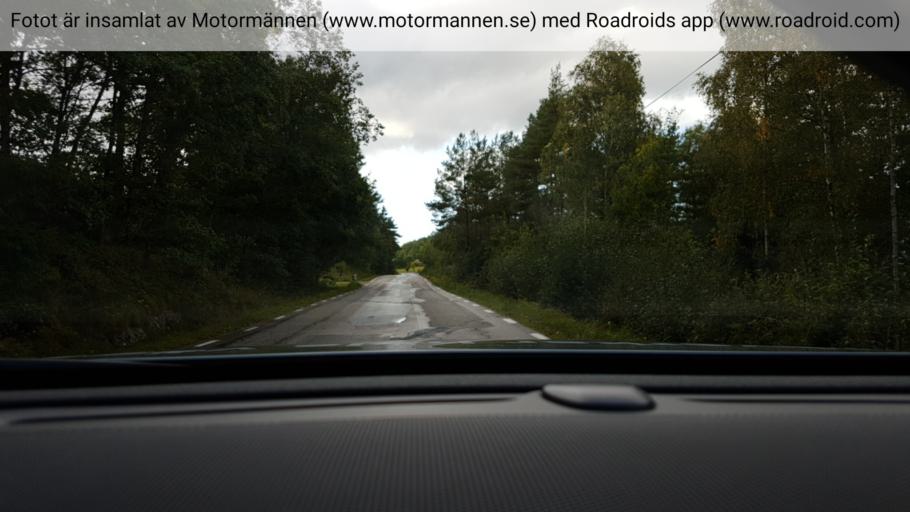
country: SE
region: Vaestra Goetaland
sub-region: Tjorns Kommun
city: Skaerhamn
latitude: 58.1285
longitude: 11.5768
